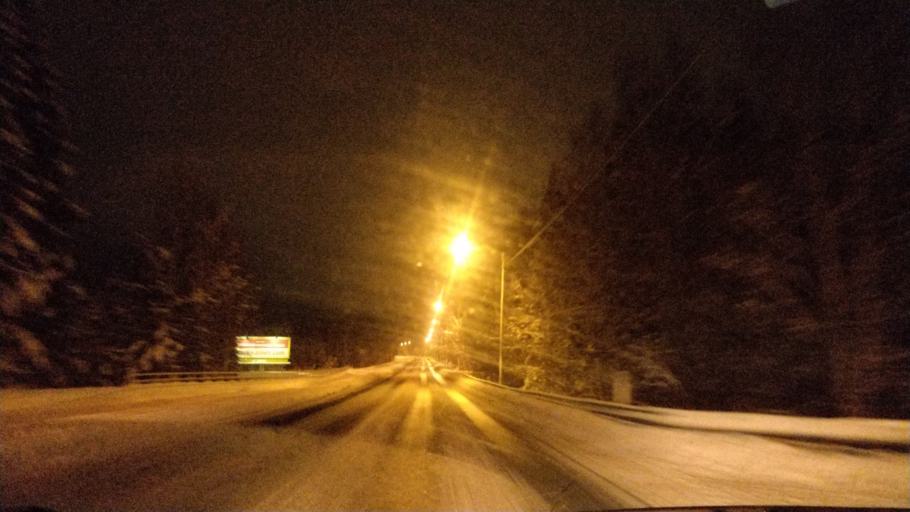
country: FI
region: Lapland
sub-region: Rovaniemi
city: Rovaniemi
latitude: 66.3837
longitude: 25.3775
